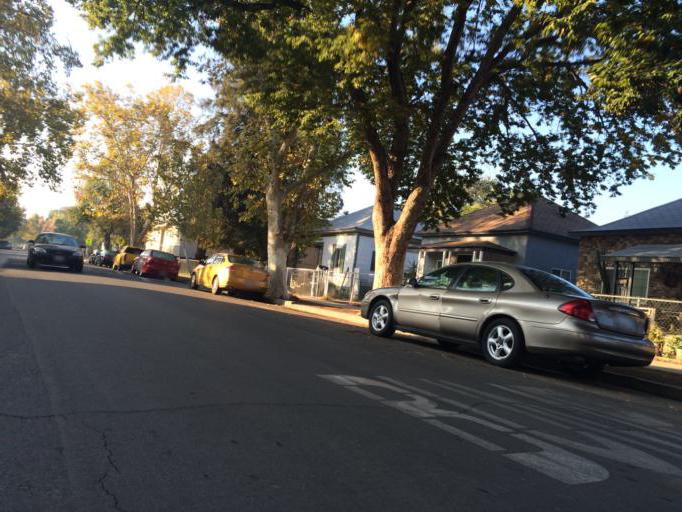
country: US
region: California
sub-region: Fresno County
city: Fresno
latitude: 36.7458
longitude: -119.7793
